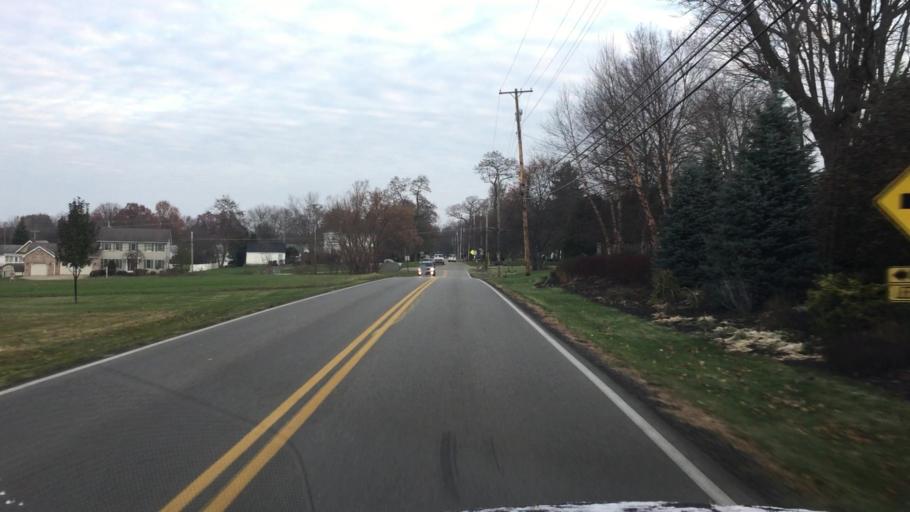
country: US
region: Ohio
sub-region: Mahoning County
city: Poland
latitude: 41.0053
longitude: -80.6100
